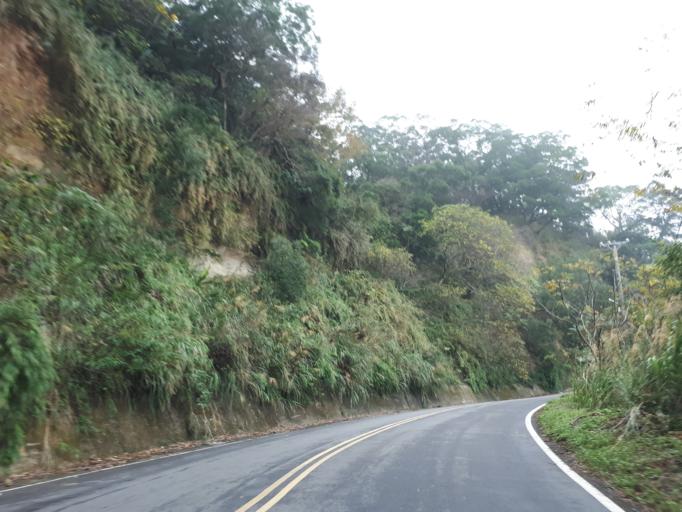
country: TW
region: Taiwan
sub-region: Hsinchu
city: Zhubei
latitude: 24.7338
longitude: 121.0801
